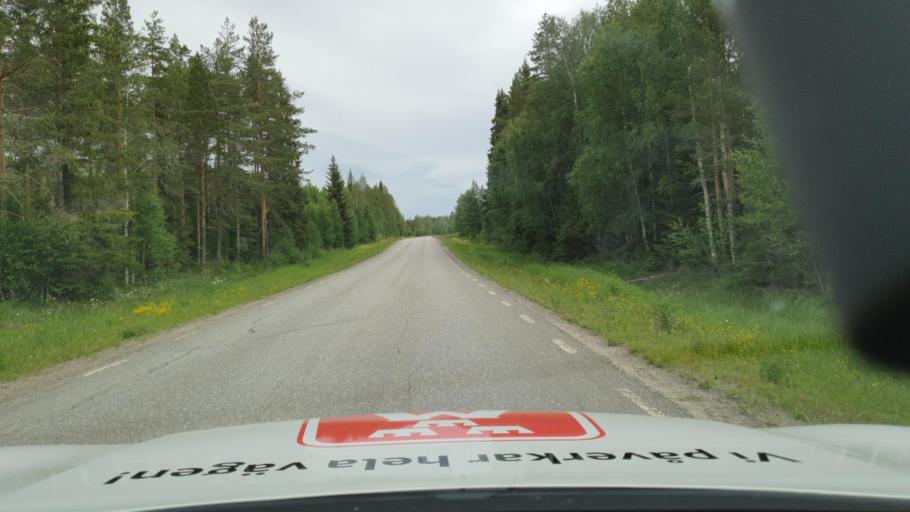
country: SE
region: Vaesterbotten
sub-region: Skelleftea Kommun
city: Burtraesk
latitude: 64.2955
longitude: 20.6458
